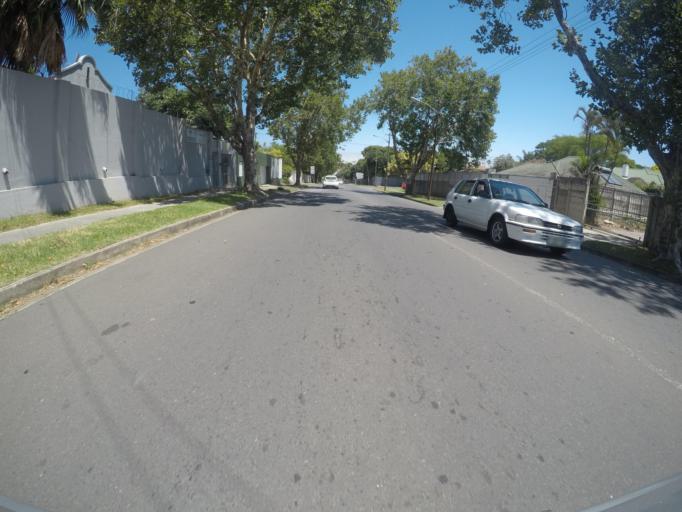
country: ZA
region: Eastern Cape
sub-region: Buffalo City Metropolitan Municipality
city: East London
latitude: -32.9871
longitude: 27.9019
